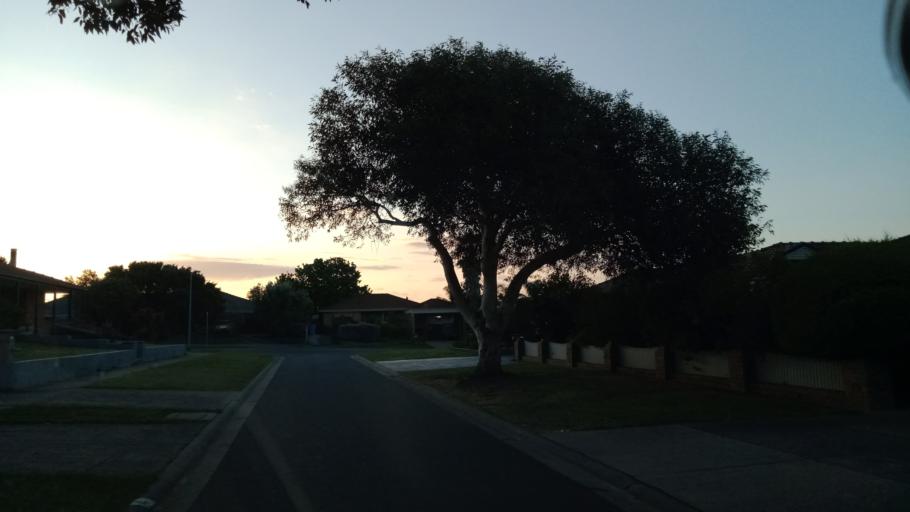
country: AU
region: Victoria
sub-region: Casey
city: Cranbourne North
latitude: -38.0838
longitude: 145.2717
